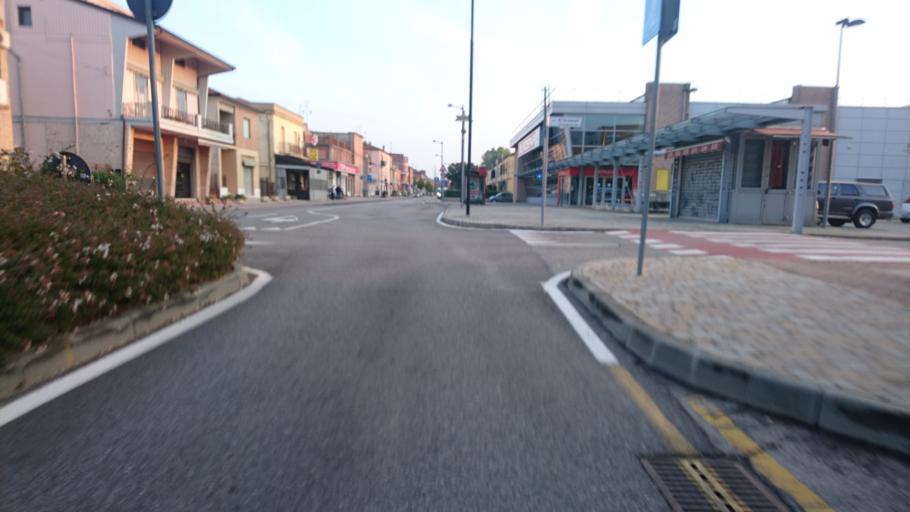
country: IT
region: Emilia-Romagna
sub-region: Provincia di Ferrara
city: Ferrara
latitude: 44.8652
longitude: 11.6061
